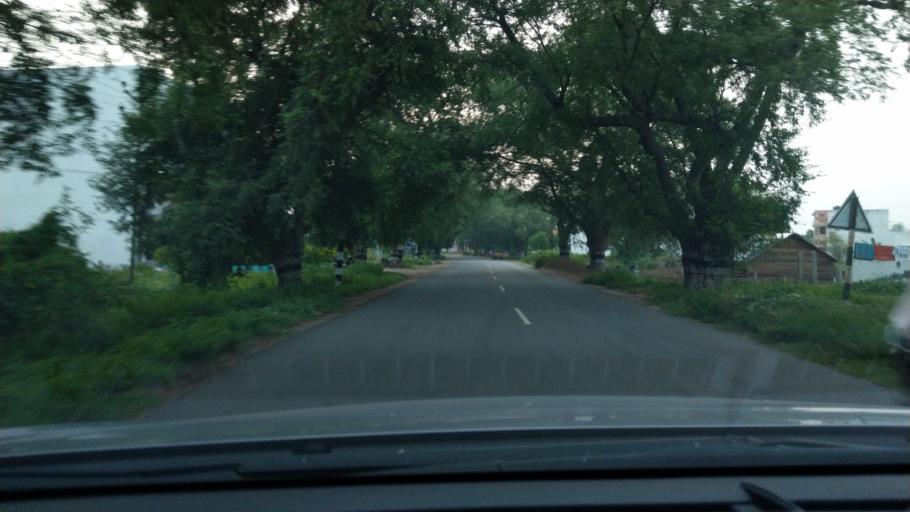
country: IN
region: Tamil Nadu
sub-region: Salem
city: Attur
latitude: 11.5945
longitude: 78.5682
